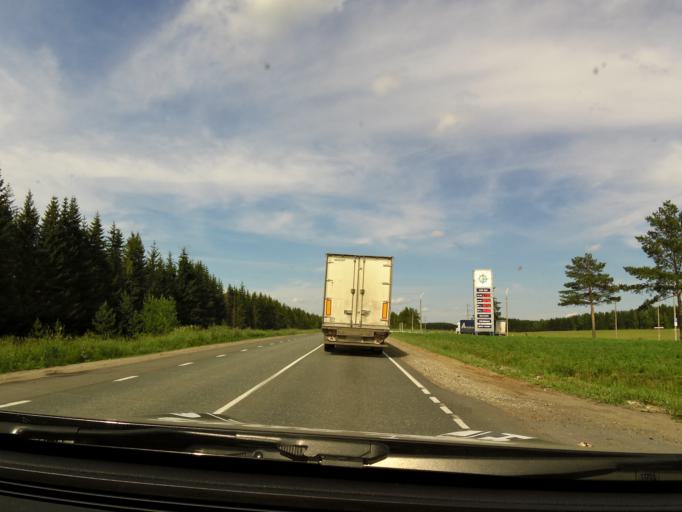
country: RU
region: Kirov
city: Slobodskoy
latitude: 58.7429
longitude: 50.3015
